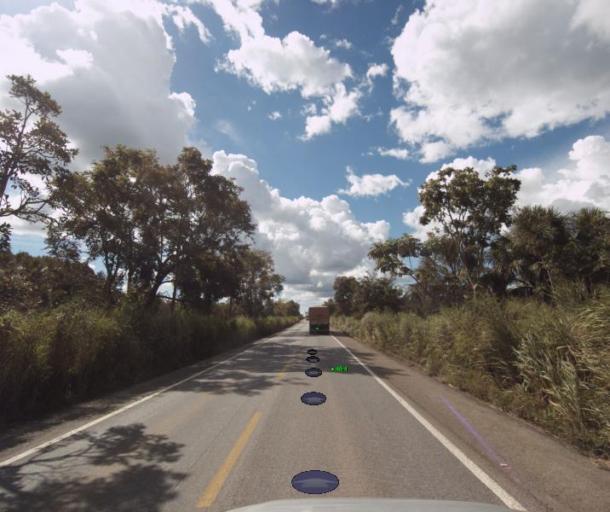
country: BR
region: Goias
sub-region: Porangatu
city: Porangatu
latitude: -13.2406
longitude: -49.1420
